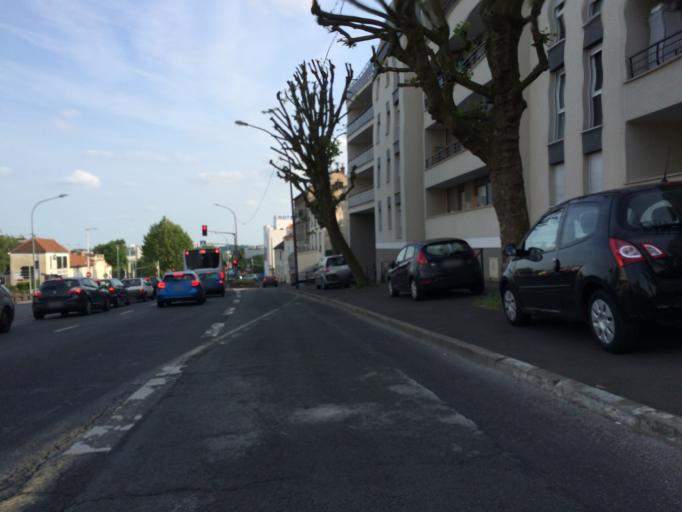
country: FR
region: Ile-de-France
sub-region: Departement de l'Essonne
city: Juvisy-sur-Orge
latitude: 48.6894
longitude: 2.3707
